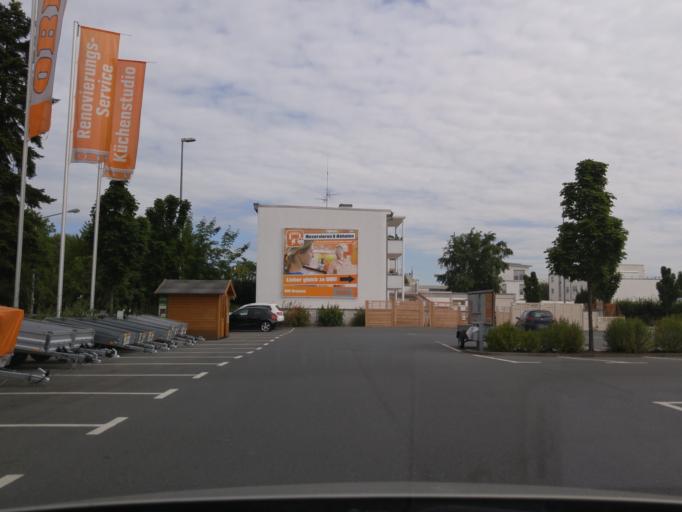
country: DE
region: Hesse
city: Dreieich
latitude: 50.0297
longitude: 8.6959
